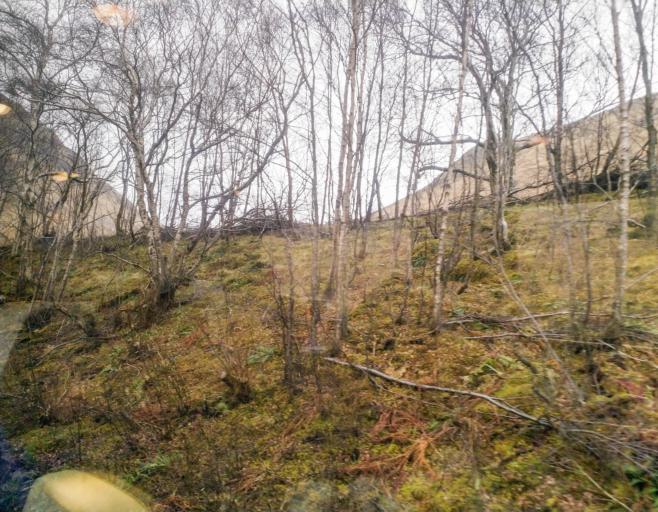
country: GB
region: Scotland
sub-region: Argyll and Bute
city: Garelochhead
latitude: 56.4813
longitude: -4.7052
